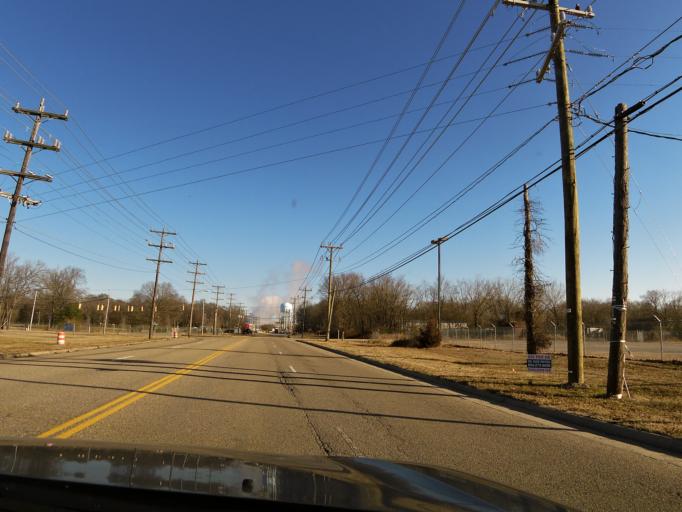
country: US
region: Virginia
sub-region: City of Hopewell
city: Hopewell
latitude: 37.2941
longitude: -77.2802
